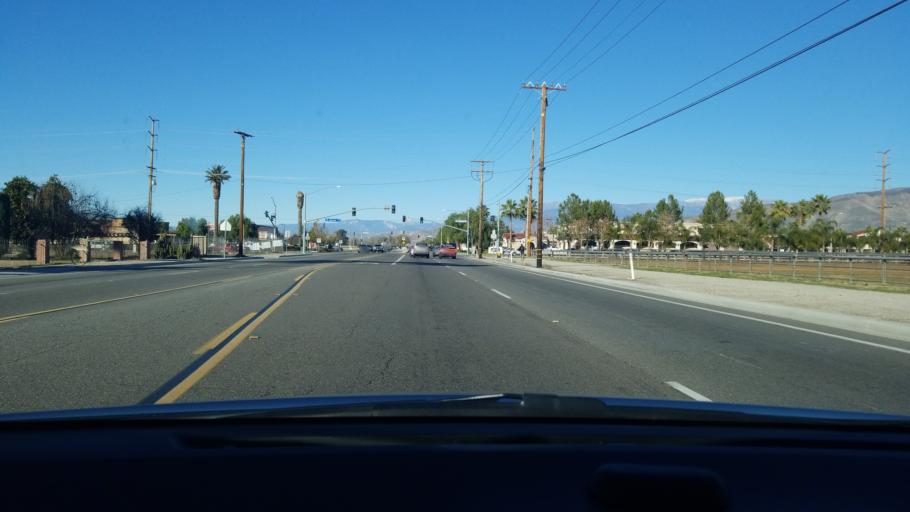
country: US
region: California
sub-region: Riverside County
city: Hemet
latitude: 33.7716
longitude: -117.0067
